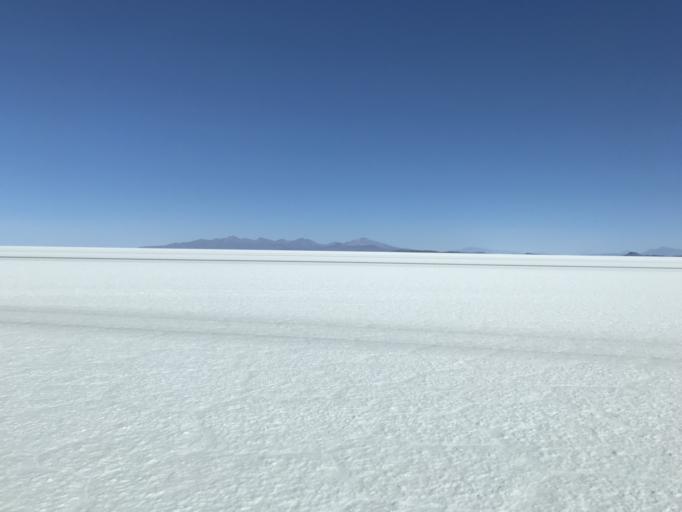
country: BO
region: Potosi
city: Colchani
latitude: -20.2389
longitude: -67.6161
